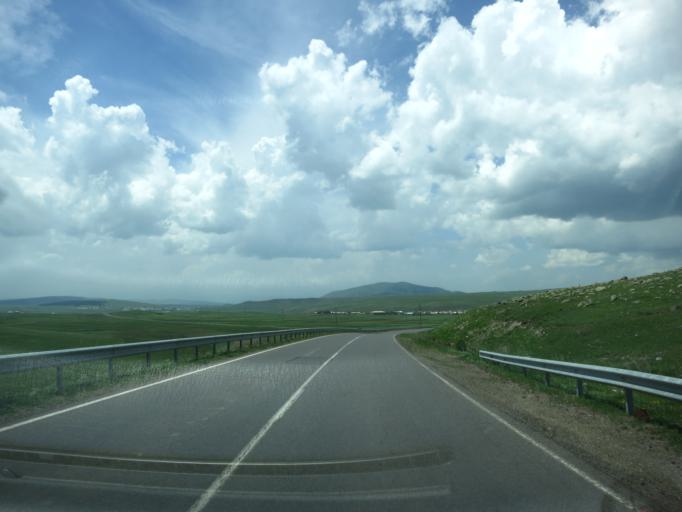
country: GE
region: Samtskhe-Javakheti
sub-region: Ninotsminda
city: Ninotsminda
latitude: 41.2951
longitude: 43.6765
